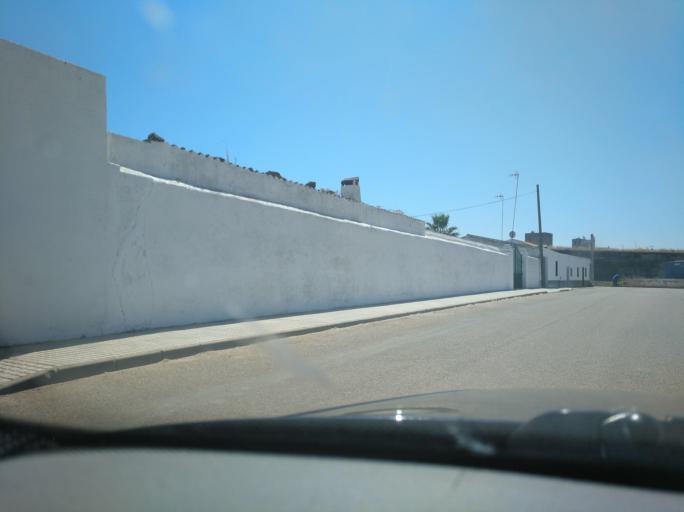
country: ES
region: Extremadura
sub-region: Provincia de Badajoz
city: Olivenza
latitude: 38.6886
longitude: -7.1030
